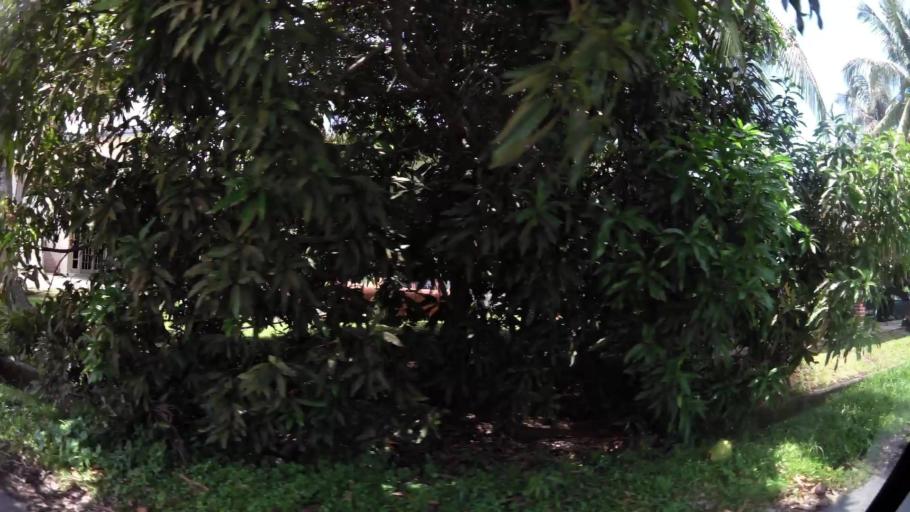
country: BN
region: Belait
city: Kuala Belait
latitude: 4.5848
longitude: 114.2402
